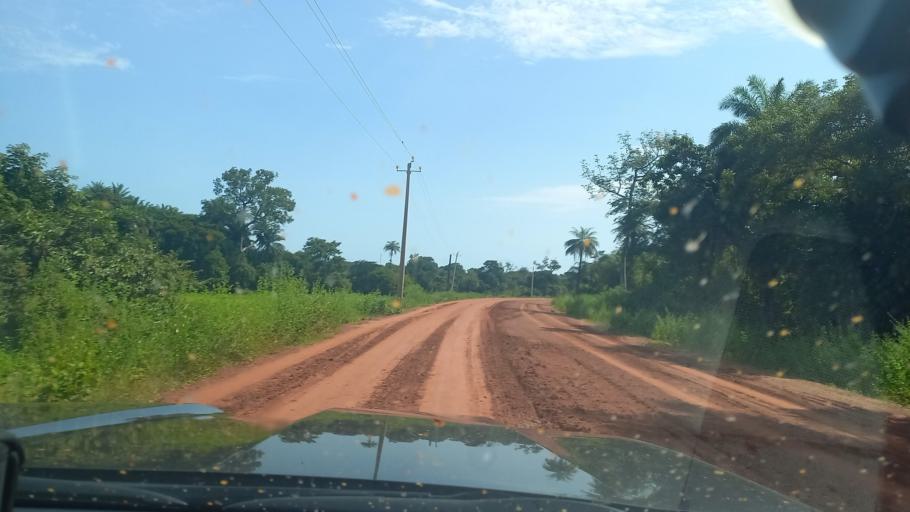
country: SN
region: Ziguinchor
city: Adeane
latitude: 12.6664
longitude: -16.1029
